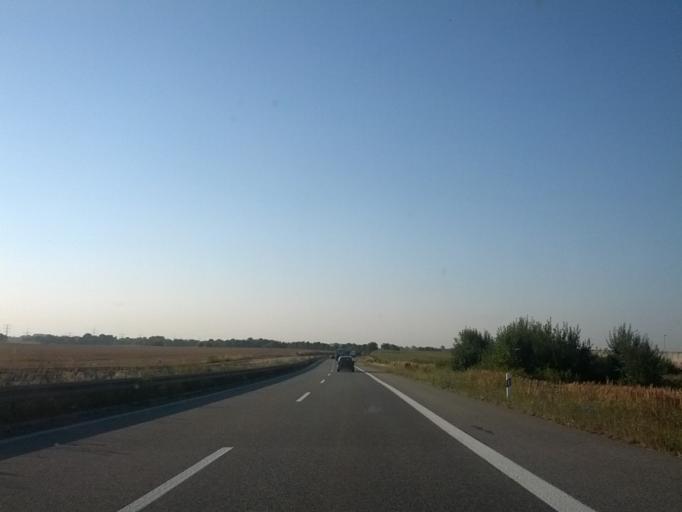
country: DE
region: Mecklenburg-Vorpommern
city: Wendorf
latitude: 54.2809
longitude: 13.0752
